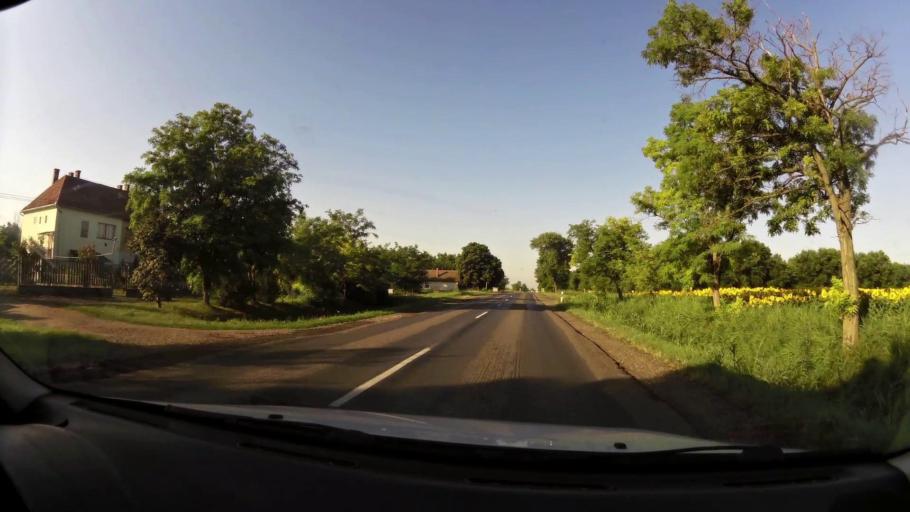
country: HU
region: Pest
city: Cegled
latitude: 47.2262
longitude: 19.8325
